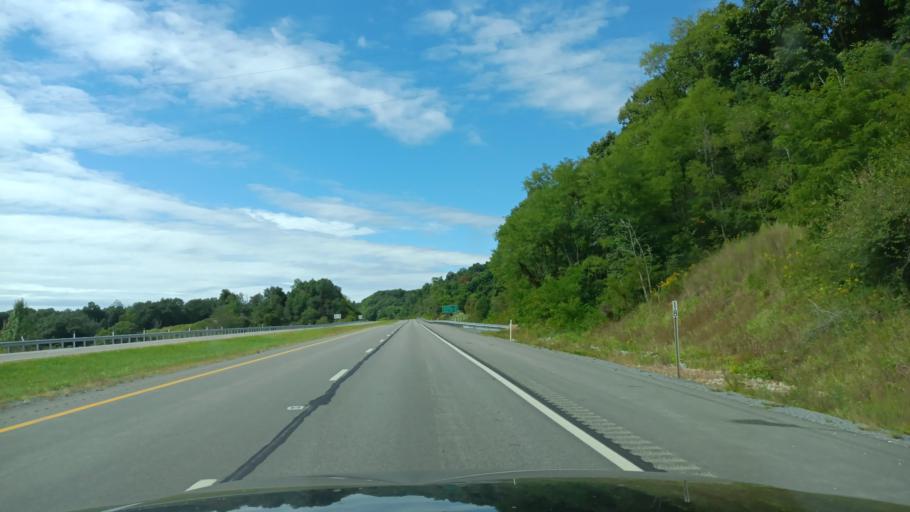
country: US
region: West Virginia
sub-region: Ritchie County
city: Pennsboro
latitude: 39.2734
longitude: -80.9628
